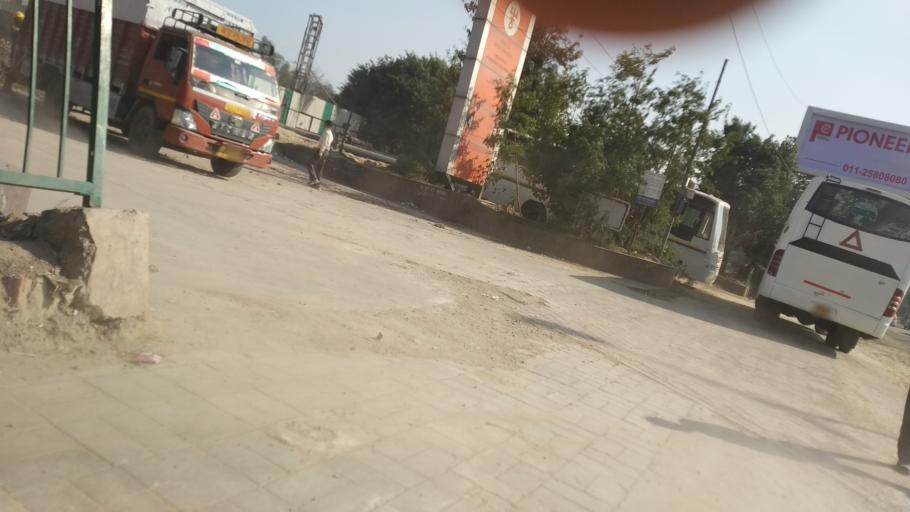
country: IN
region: NCT
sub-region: New Delhi
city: New Delhi
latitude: 28.6162
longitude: 77.2404
